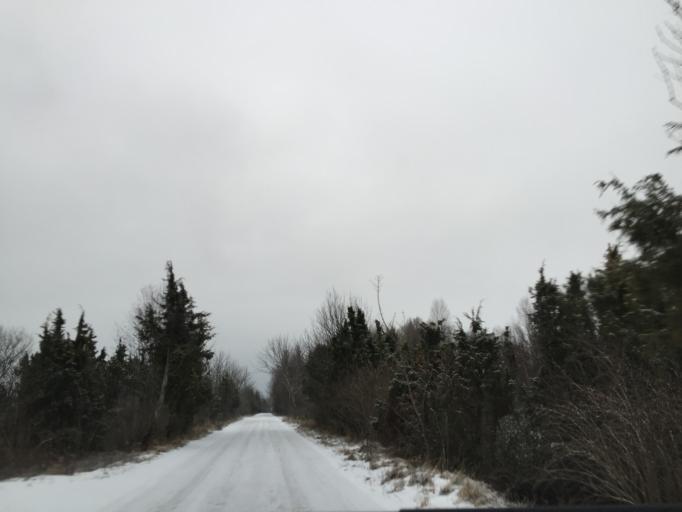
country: EE
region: Saare
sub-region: Orissaare vald
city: Orissaare
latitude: 58.5528
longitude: 23.3896
